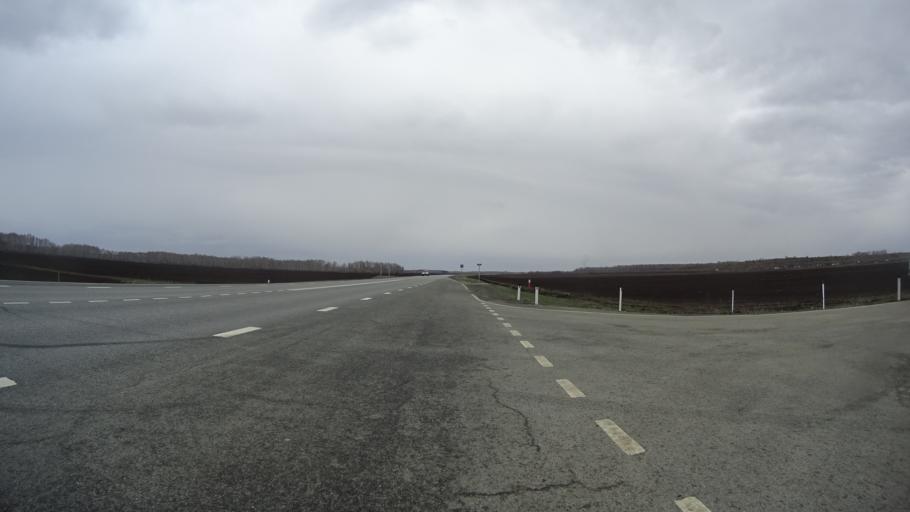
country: RU
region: Chelyabinsk
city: Krasnogorskiy
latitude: 54.5809
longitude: 61.2913
